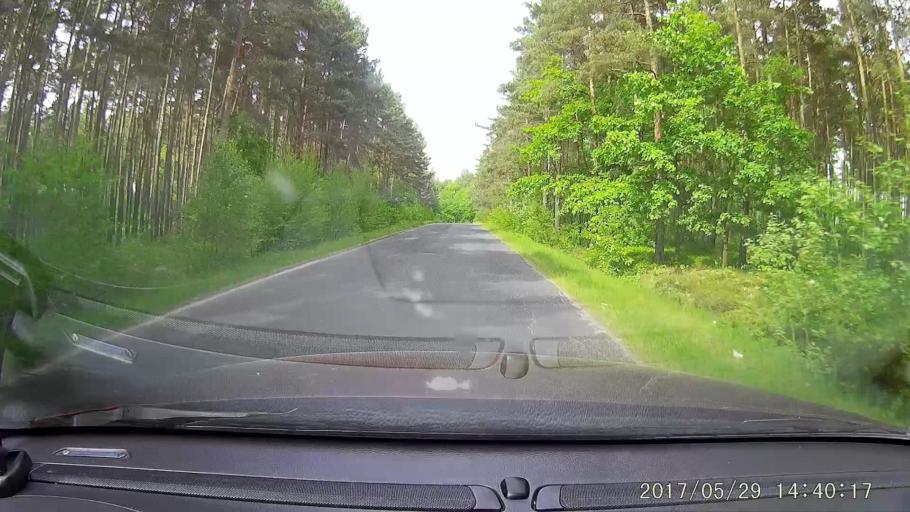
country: PL
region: Lower Silesian Voivodeship
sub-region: Powiat zgorzelecki
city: Wegliniec
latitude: 51.2239
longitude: 15.2071
